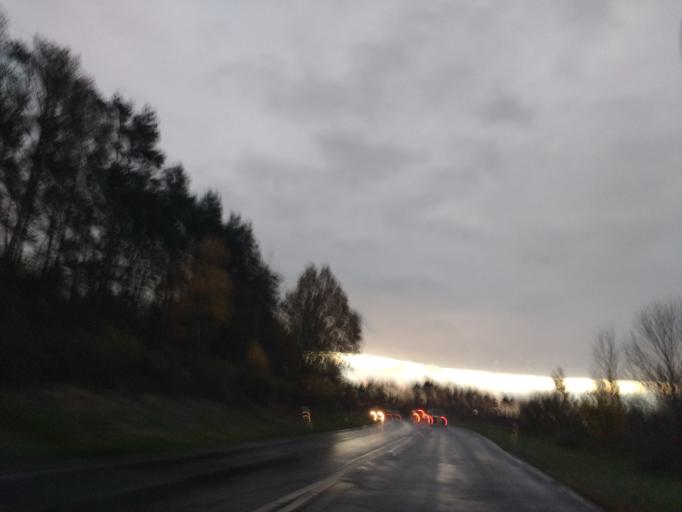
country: DE
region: Hesse
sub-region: Regierungsbezirk Kassel
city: Baunatal
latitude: 51.2525
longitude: 9.4224
